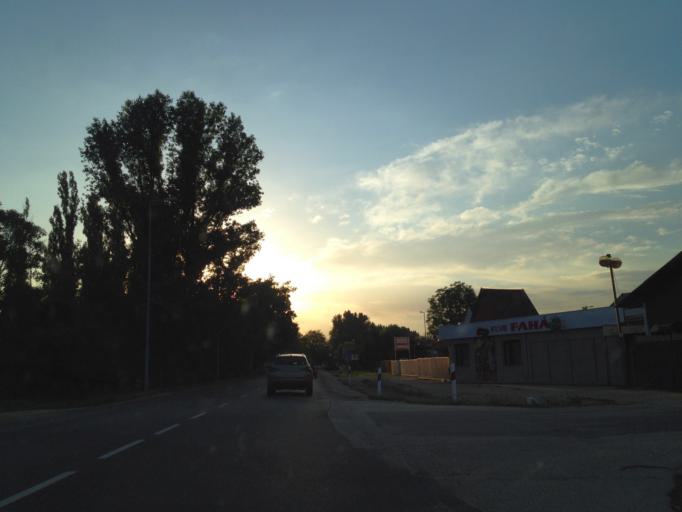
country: HU
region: Gyor-Moson-Sopron
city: Mosonmagyarovar
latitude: 47.8410
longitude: 17.2882
